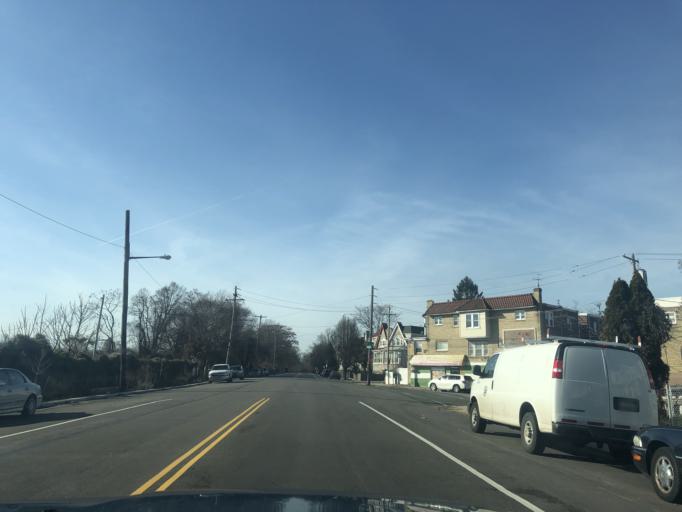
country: US
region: Pennsylvania
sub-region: Montgomery County
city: Bala-Cynwyd
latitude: 39.9852
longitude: -75.2392
